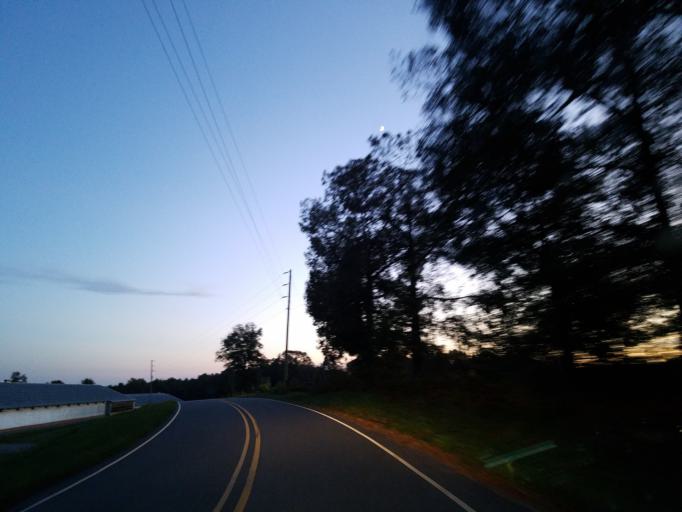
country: US
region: Georgia
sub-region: Dawson County
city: Dawsonville
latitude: 34.5241
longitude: -84.1780
